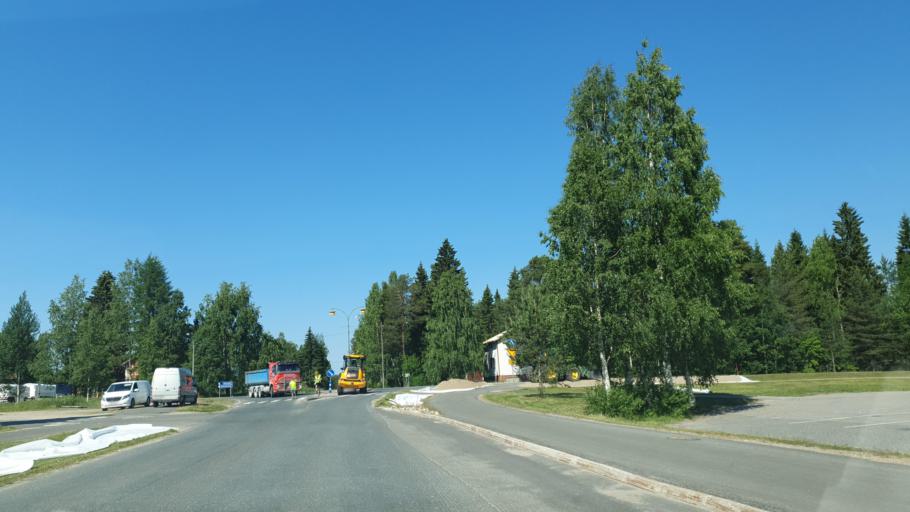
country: FI
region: Lapland
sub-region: Rovaniemi
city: Ranua
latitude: 65.9326
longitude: 26.5094
